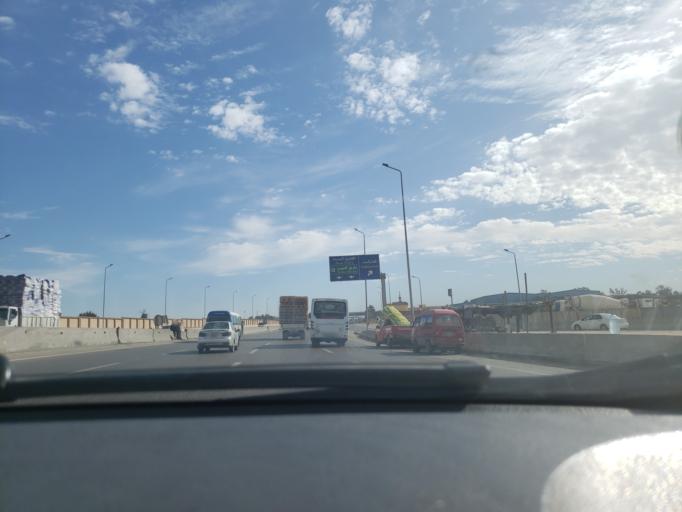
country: EG
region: Muhafazat al Qalyubiyah
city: Al Khankah
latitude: 30.1470
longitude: 31.4344
